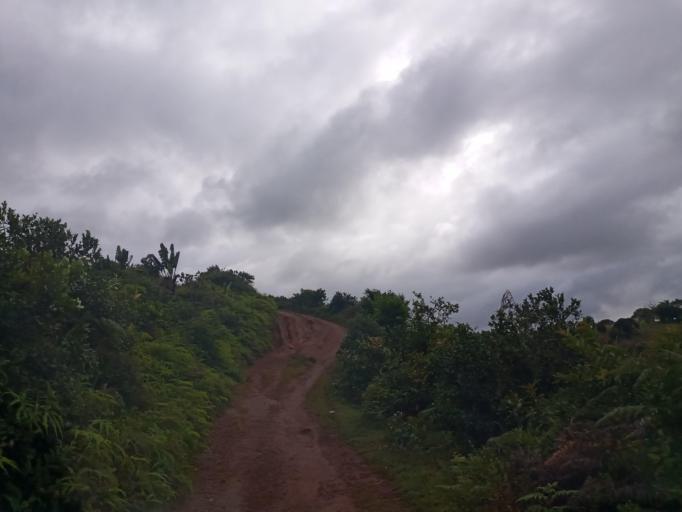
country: MG
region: Atsimo-Atsinanana
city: Vohipaho
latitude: -23.7772
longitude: 47.5362
